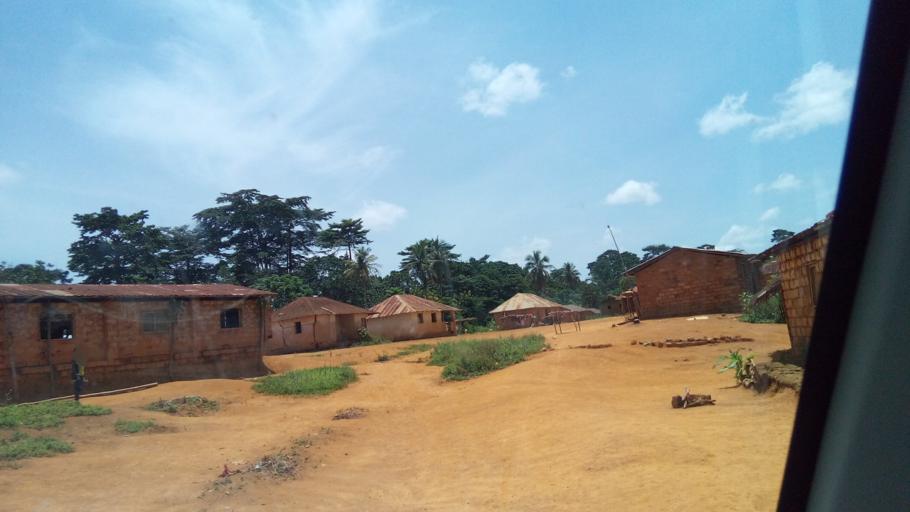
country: AO
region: Zaire
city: Mbanza Congo
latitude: -5.8029
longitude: 14.2452
